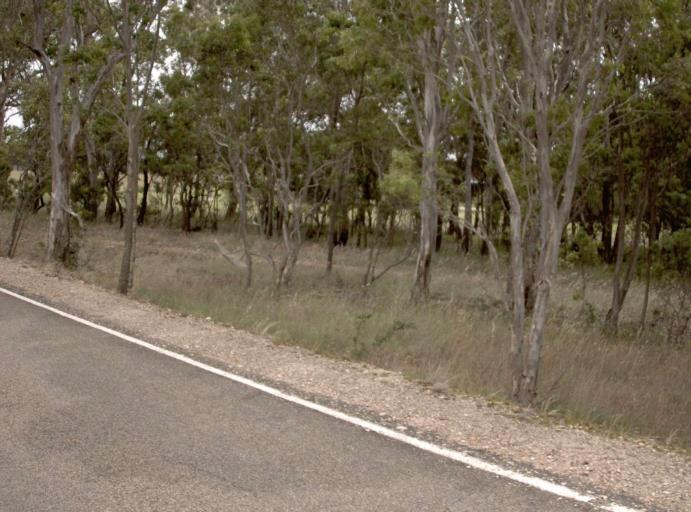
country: AU
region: Victoria
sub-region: Wellington
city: Sale
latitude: -37.9329
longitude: 147.0959
